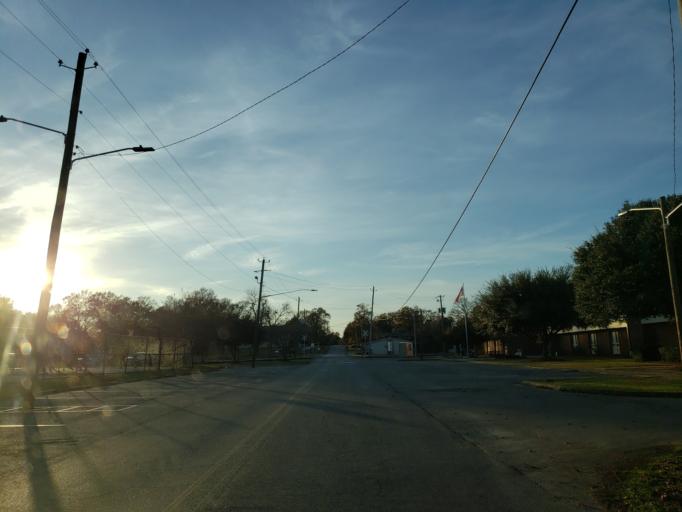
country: US
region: Mississippi
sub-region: Forrest County
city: Hattiesburg
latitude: 31.3333
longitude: -89.2921
